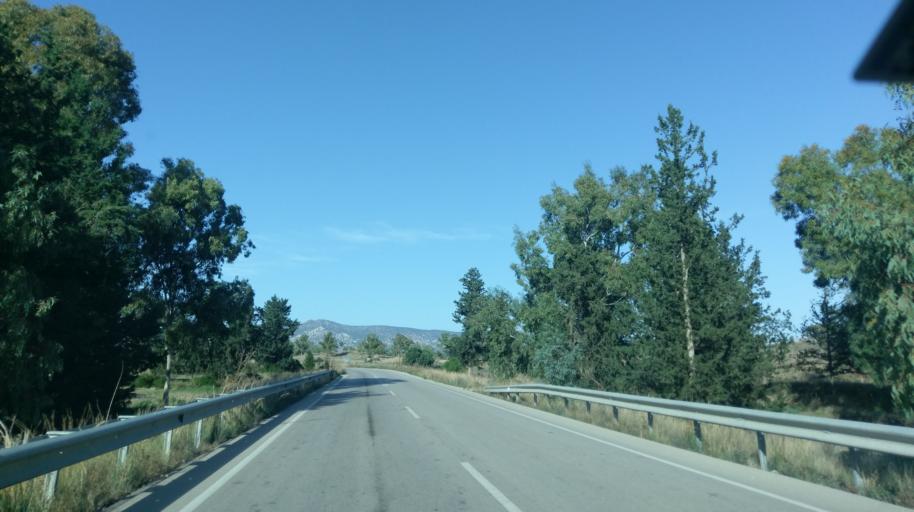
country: CY
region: Ammochostos
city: Lefkonoiko
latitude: 35.2866
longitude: 33.7366
